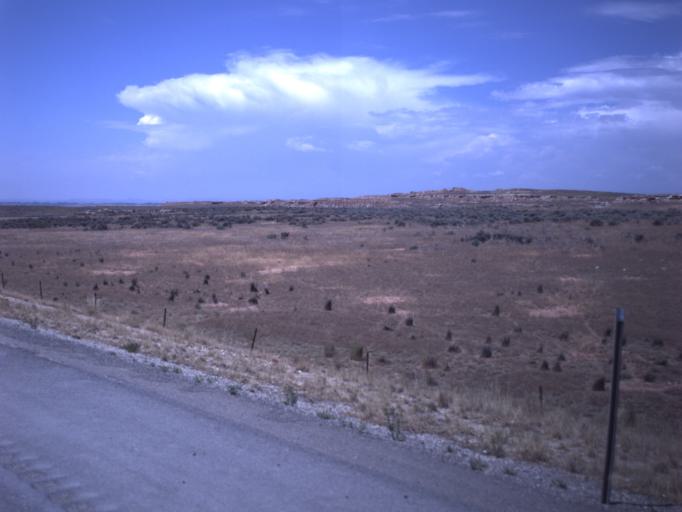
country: US
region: Utah
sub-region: Uintah County
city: Maeser
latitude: 40.3135
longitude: -109.7411
